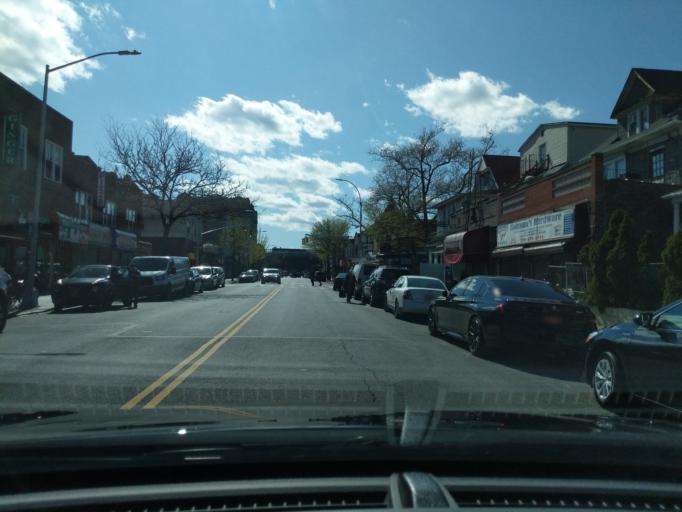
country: US
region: New York
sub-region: Kings County
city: Brooklyn
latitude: 40.6359
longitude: -73.9752
